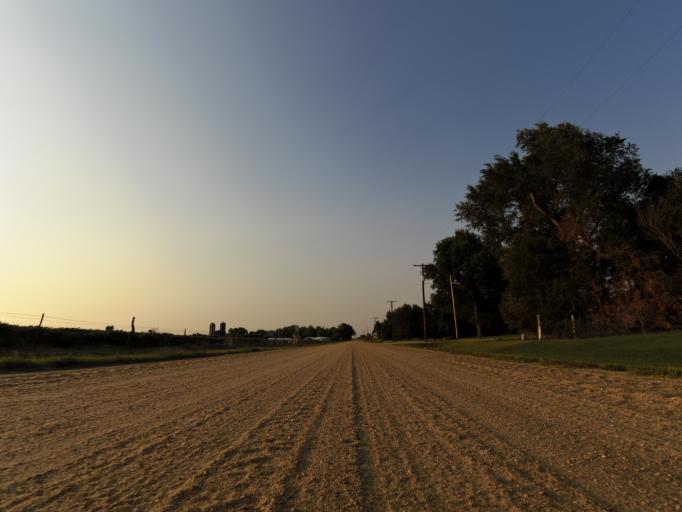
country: US
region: Kansas
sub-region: Reno County
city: South Hutchinson
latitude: 38.0097
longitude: -97.9954
